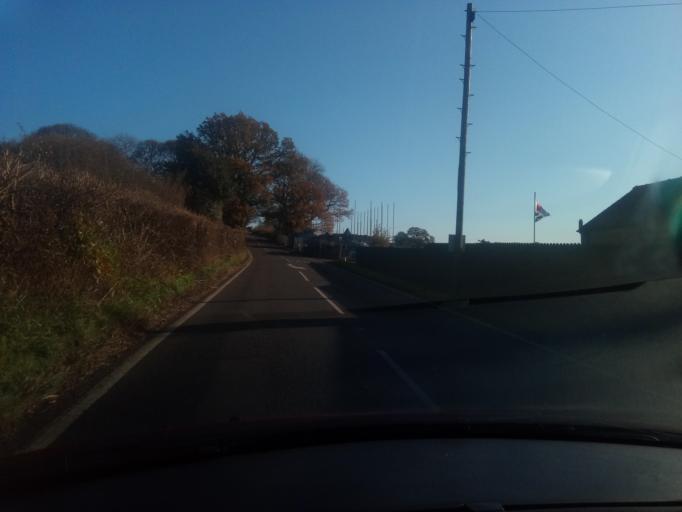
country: GB
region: England
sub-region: Derbyshire
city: Belper
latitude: 53.0227
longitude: -1.5329
